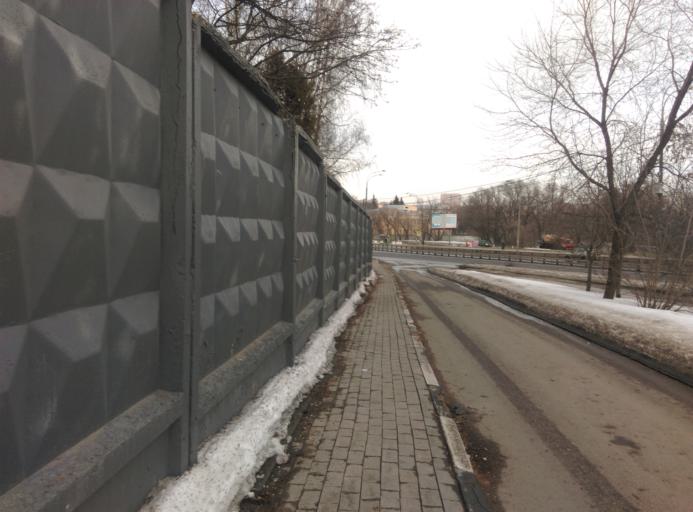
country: RU
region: Moskovskaya
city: Bol'shaya Setun'
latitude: 55.7091
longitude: 37.4210
